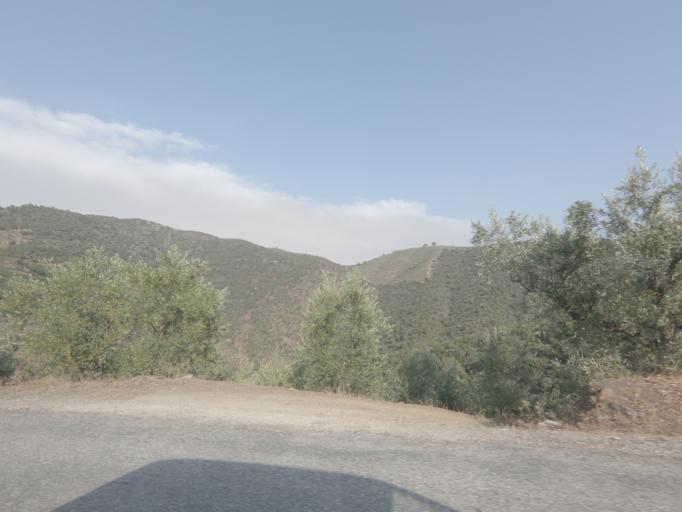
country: PT
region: Viseu
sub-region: Tabuaco
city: Tabuaco
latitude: 41.1231
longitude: -7.5493
